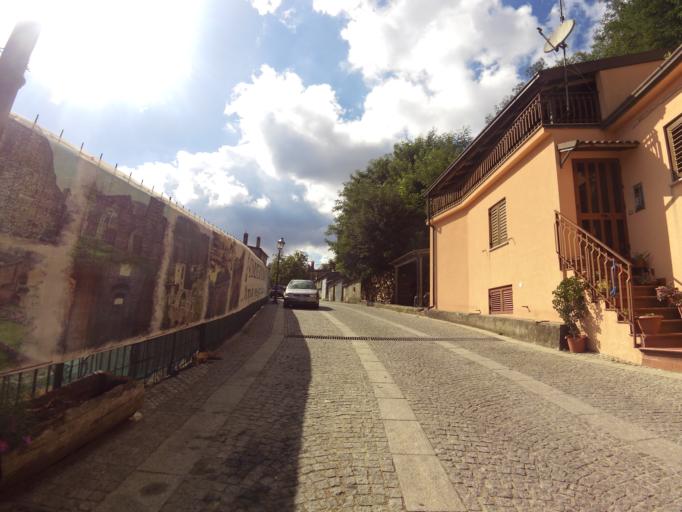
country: IT
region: Calabria
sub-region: Provincia di Vibo-Valentia
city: Mongiana
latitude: 38.5113
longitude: 16.3205
